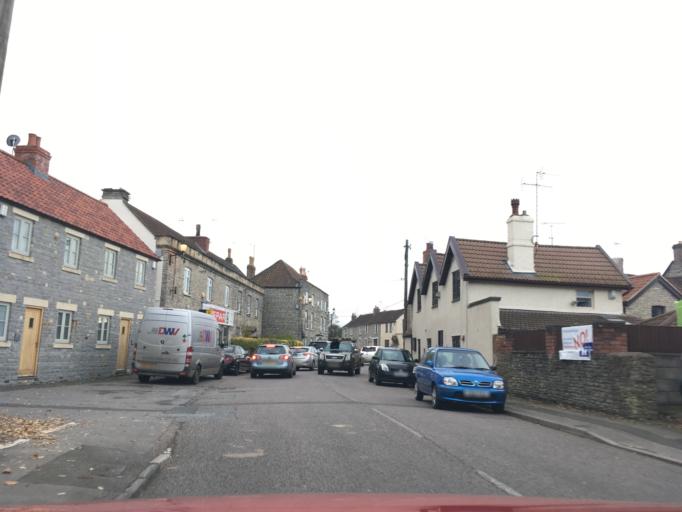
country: GB
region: England
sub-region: South Gloucestershire
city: Pucklechurch
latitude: 51.4864
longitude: -2.4346
